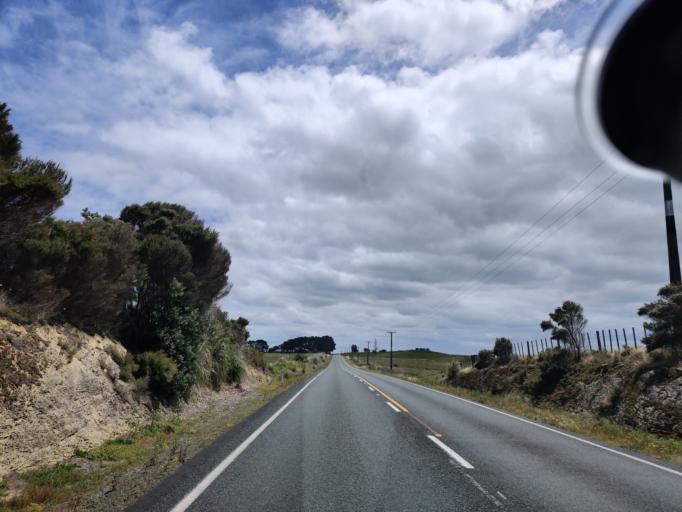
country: NZ
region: Northland
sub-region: Far North District
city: Kaitaia
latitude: -34.6991
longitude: 173.0267
